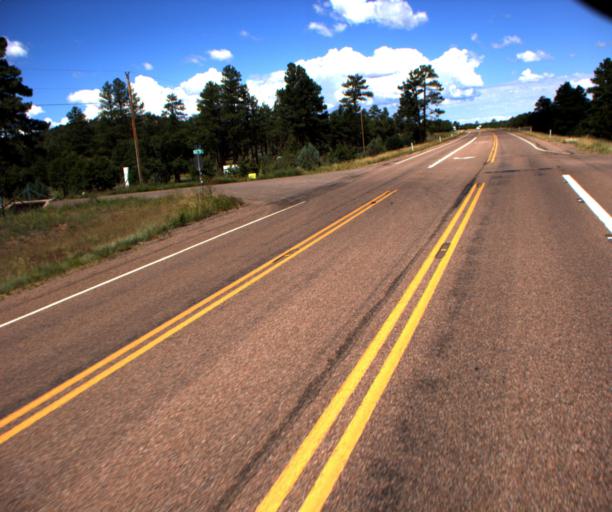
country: US
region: Arizona
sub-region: Navajo County
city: Linden
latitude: 34.3368
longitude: -110.2735
